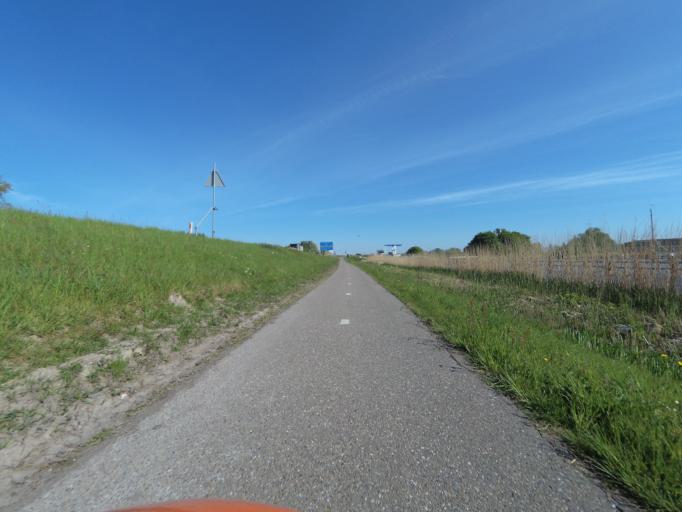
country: NL
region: Overijssel
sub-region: Gemeente Kampen
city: Kampen
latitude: 52.5419
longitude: 5.8550
